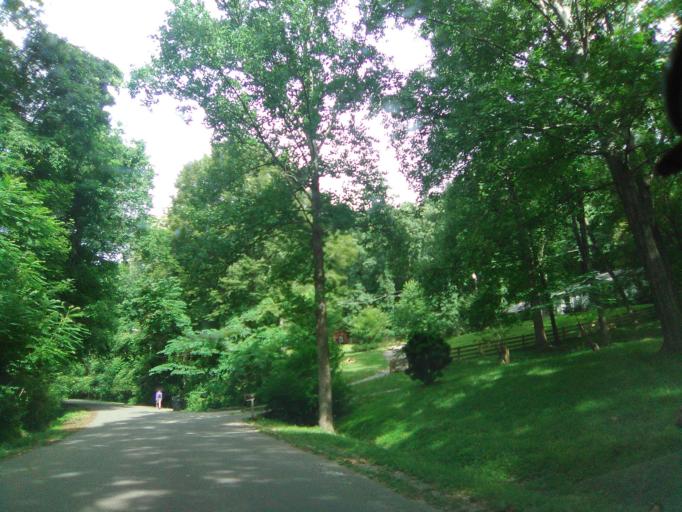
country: US
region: Tennessee
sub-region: Davidson County
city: Belle Meade
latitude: 36.0950
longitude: -86.9083
